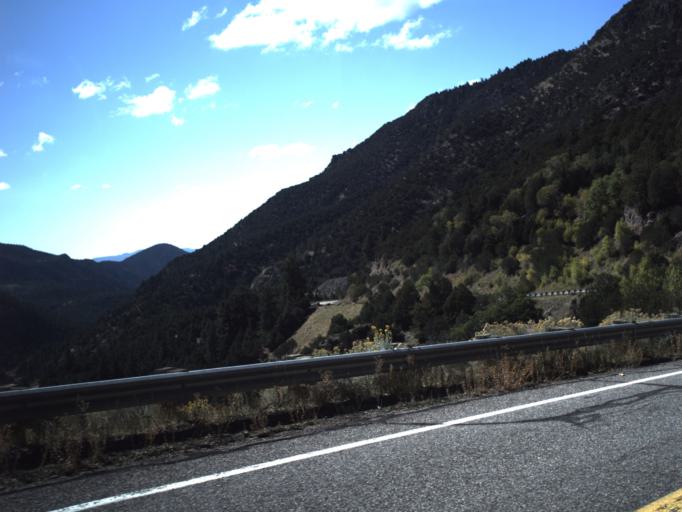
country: US
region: Utah
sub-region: Beaver County
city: Beaver
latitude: 38.2714
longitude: -112.4783
